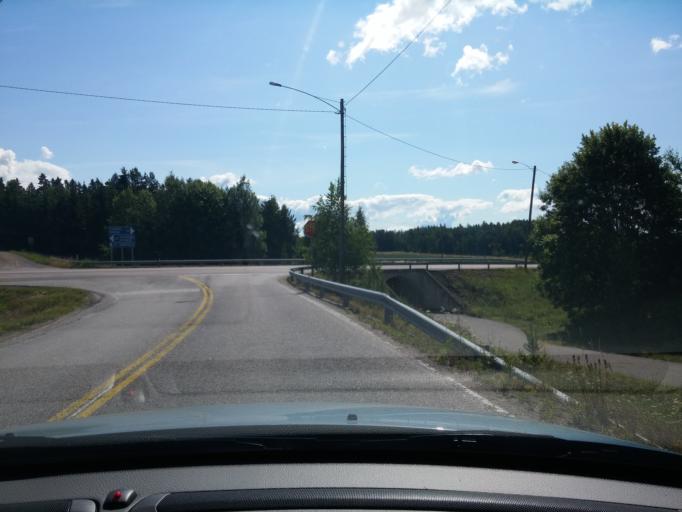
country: FI
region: Uusimaa
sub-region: Porvoo
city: Askola
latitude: 60.4490
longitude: 25.5847
